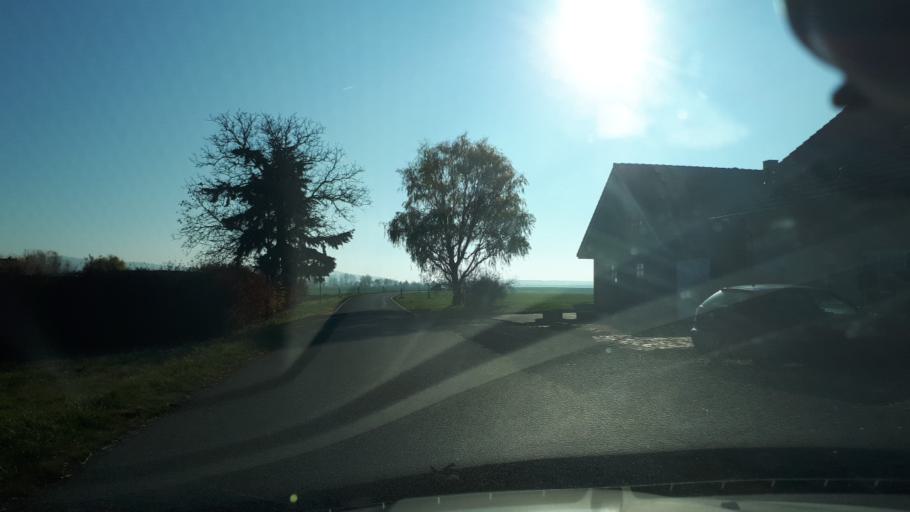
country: DE
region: Rheinland-Pfalz
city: Brieden
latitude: 50.1858
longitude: 7.2643
